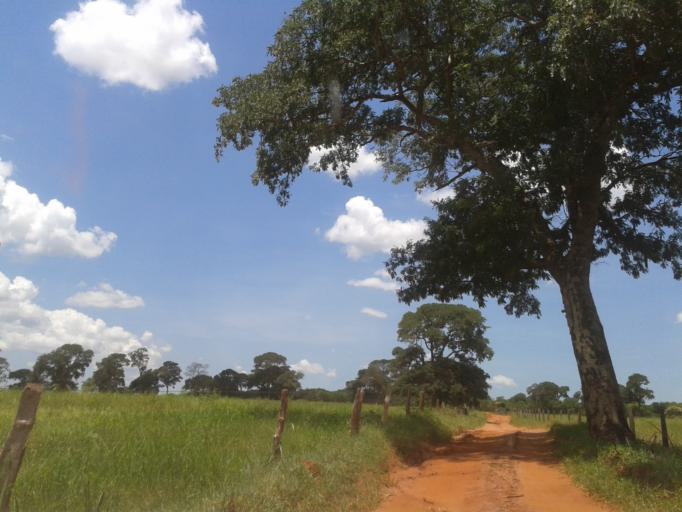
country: BR
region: Minas Gerais
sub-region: Santa Vitoria
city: Santa Vitoria
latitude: -19.2079
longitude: -50.3985
